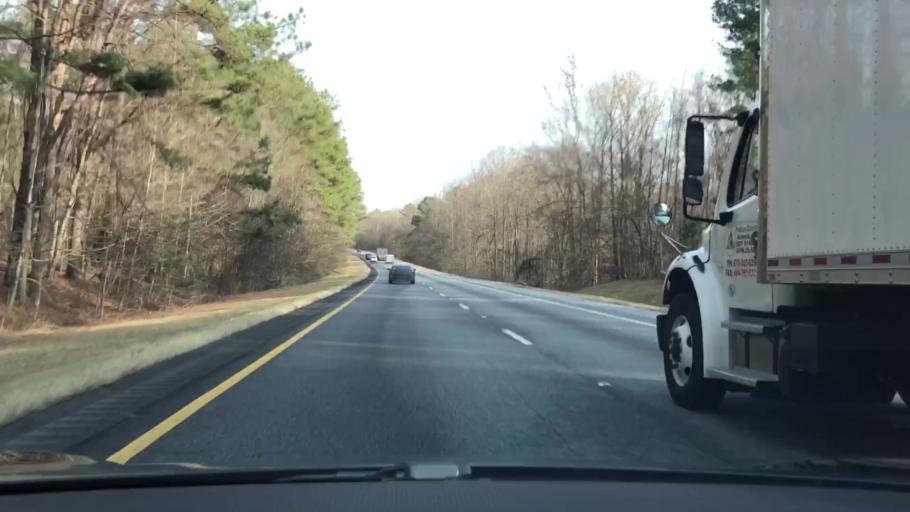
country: US
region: Georgia
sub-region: Morgan County
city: Madison
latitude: 33.5763
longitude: -83.5685
